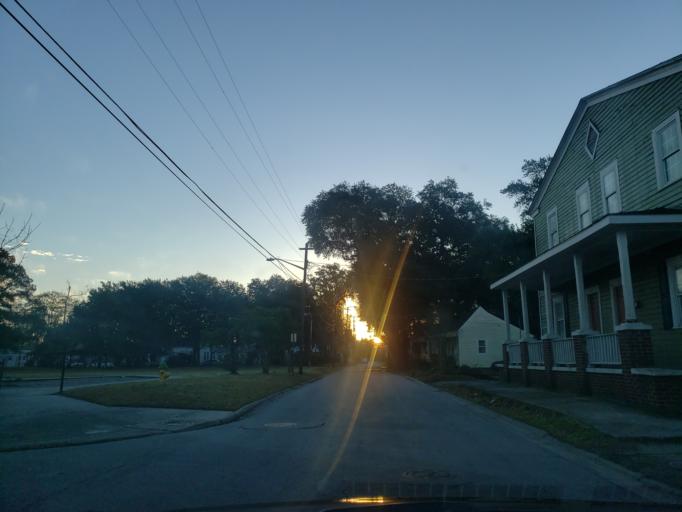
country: US
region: Georgia
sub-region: Chatham County
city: Savannah
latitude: 32.0425
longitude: -81.1089
